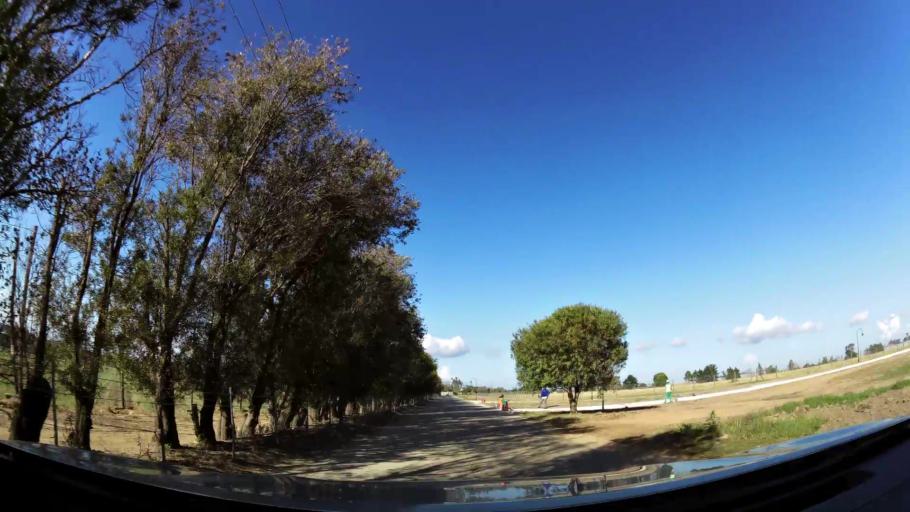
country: ZA
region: Western Cape
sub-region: Eden District Municipality
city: George
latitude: -33.9590
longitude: 22.3988
